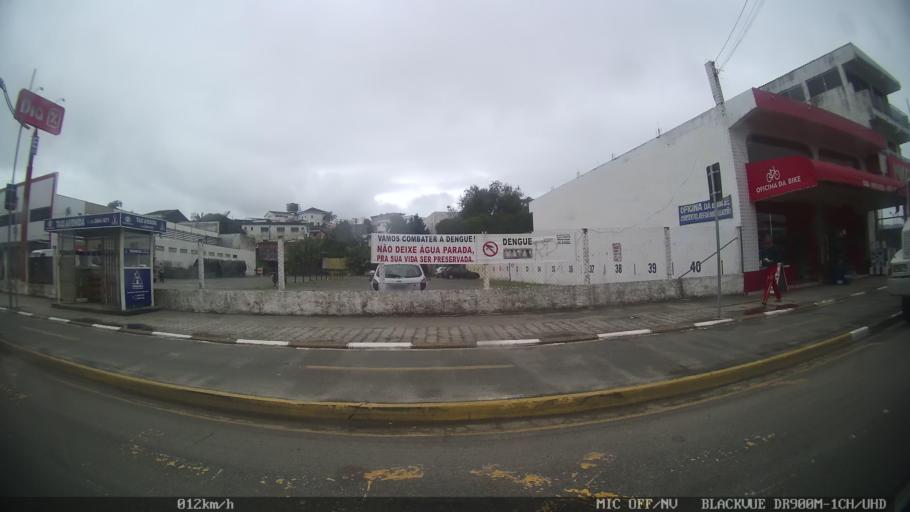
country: BR
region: Sao Paulo
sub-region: Juquia
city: Juquia
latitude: -24.3206
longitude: -47.6366
